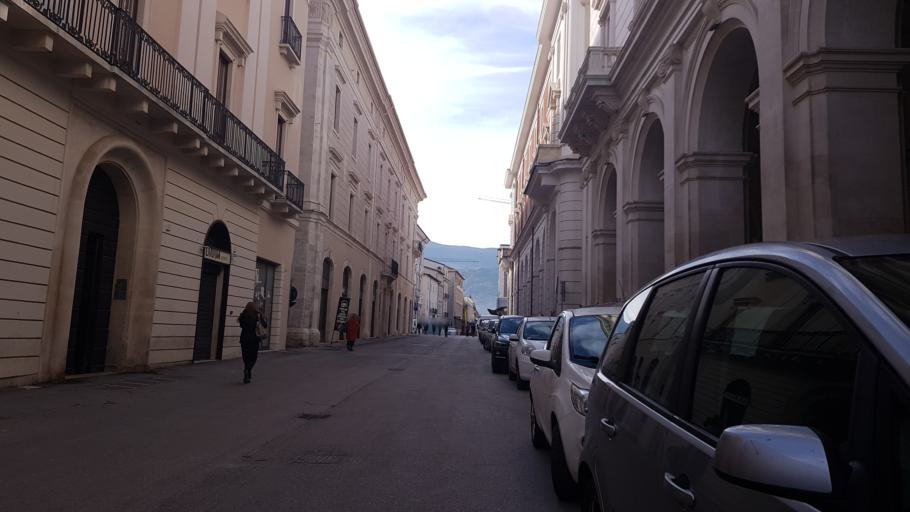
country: IT
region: Abruzzo
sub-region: Provincia dell' Aquila
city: L'Aquila
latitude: 42.3497
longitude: 13.3993
